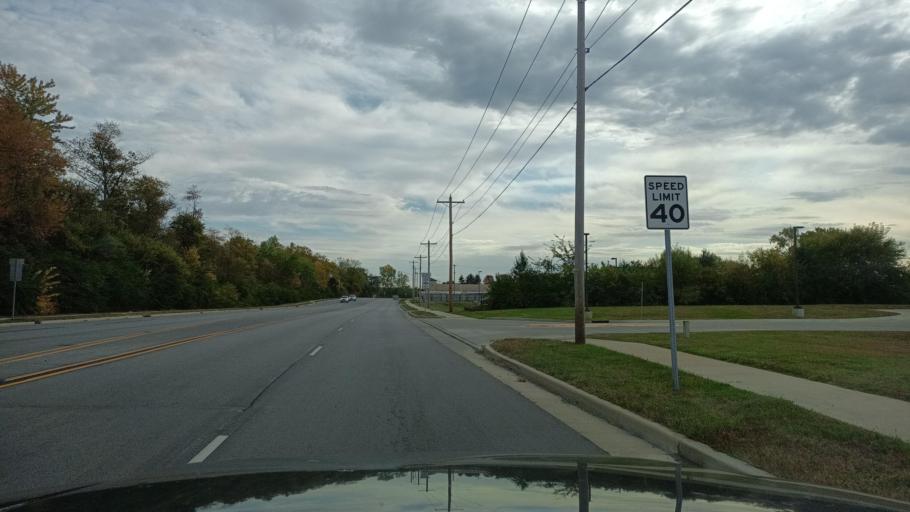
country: US
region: Indiana
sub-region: Delaware County
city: Yorktown
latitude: 40.1805
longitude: -85.4803
